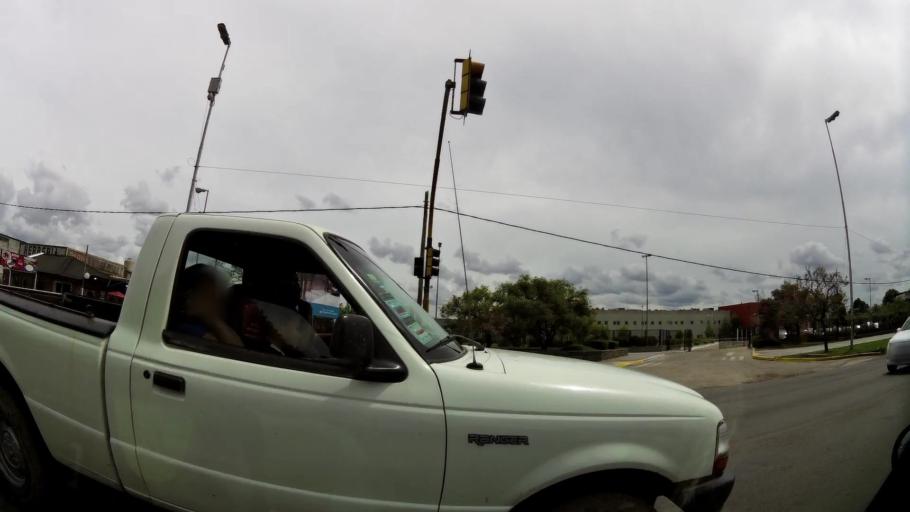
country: AR
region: Buenos Aires
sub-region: Partido de Quilmes
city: Quilmes
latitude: -34.7718
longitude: -58.2685
